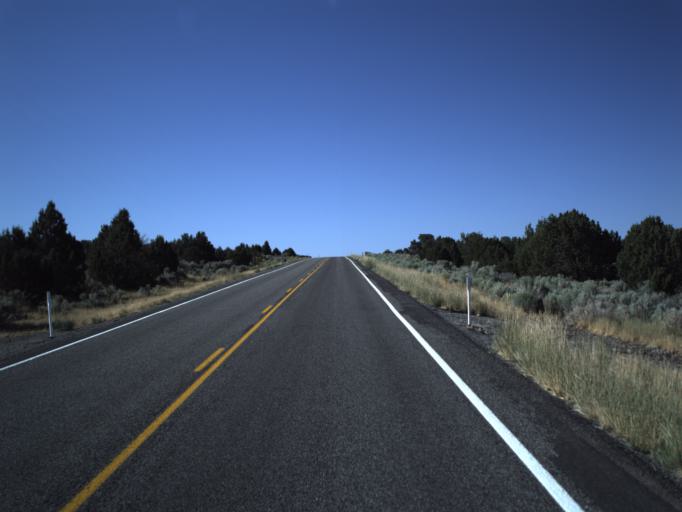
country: US
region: Utah
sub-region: Juab County
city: Mona
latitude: 39.8452
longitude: -112.1382
